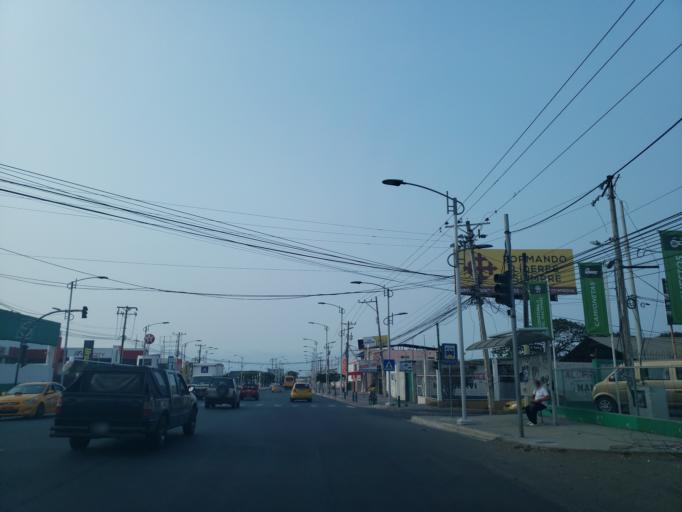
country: EC
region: Manabi
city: Manta
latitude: -0.9765
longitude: -80.6985
